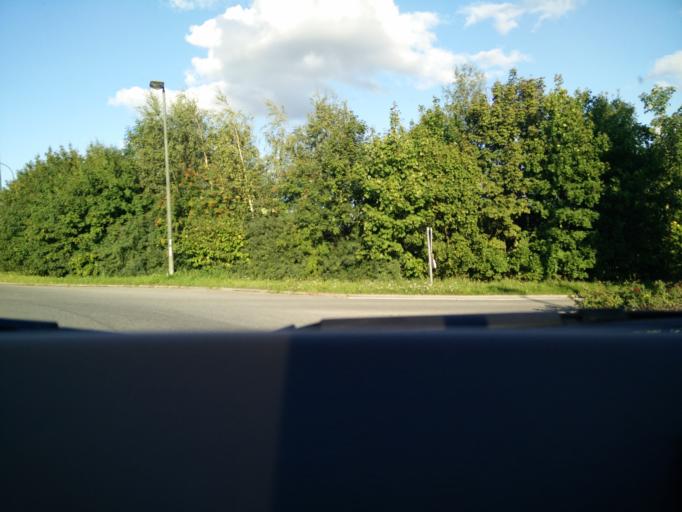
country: BE
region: Wallonia
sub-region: Province de Namur
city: Florennes
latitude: 50.2075
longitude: 4.5917
